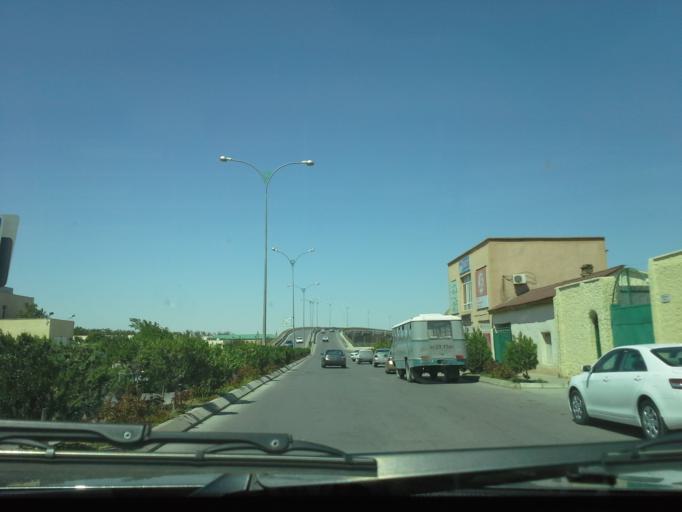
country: TM
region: Balkan
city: Serdar
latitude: 38.9760
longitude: 56.2778
